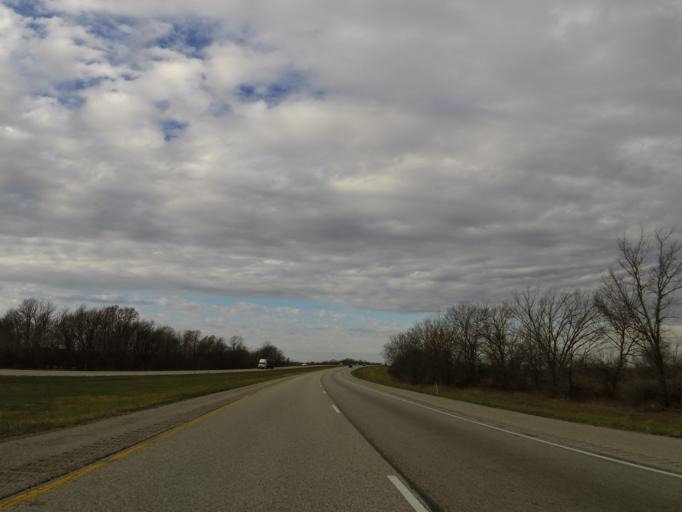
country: US
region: Illinois
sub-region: Washington County
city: Nashville
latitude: 38.3899
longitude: -89.3280
